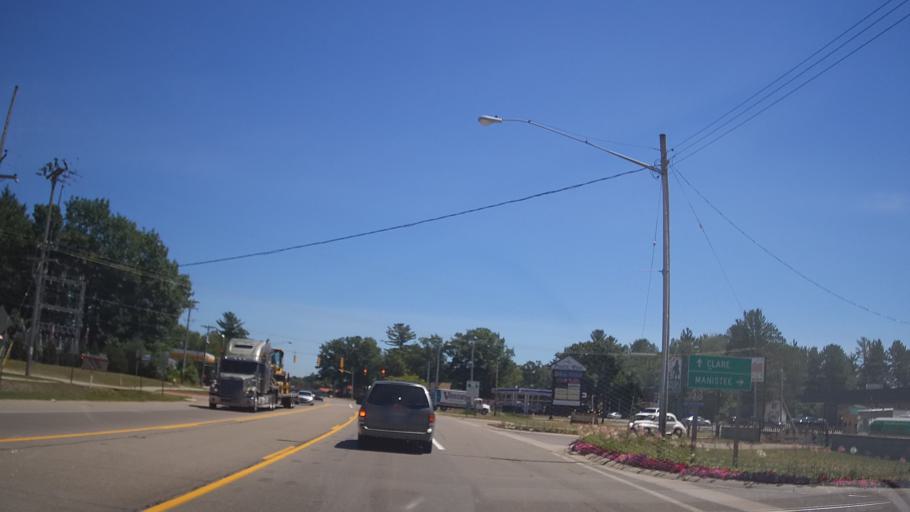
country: US
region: Michigan
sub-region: Wexford County
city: Cadillac
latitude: 44.2368
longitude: -85.4540
